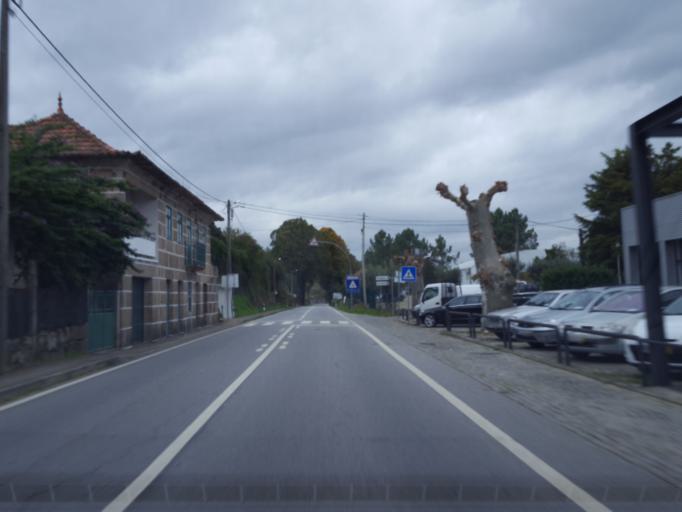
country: PT
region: Porto
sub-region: Marco de Canaveses
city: Marco de Canavezes
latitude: 41.1592
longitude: -8.1448
